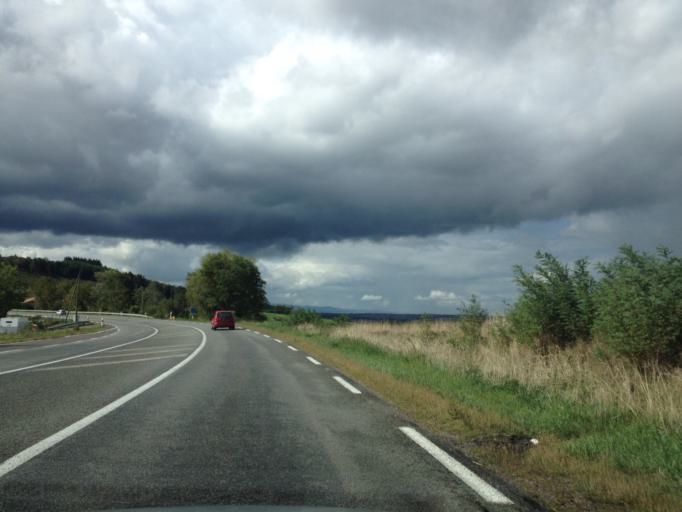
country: FR
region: Rhone-Alpes
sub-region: Departement de la Loire
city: Saint-Just-la-Pendue
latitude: 45.9426
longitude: 4.2671
